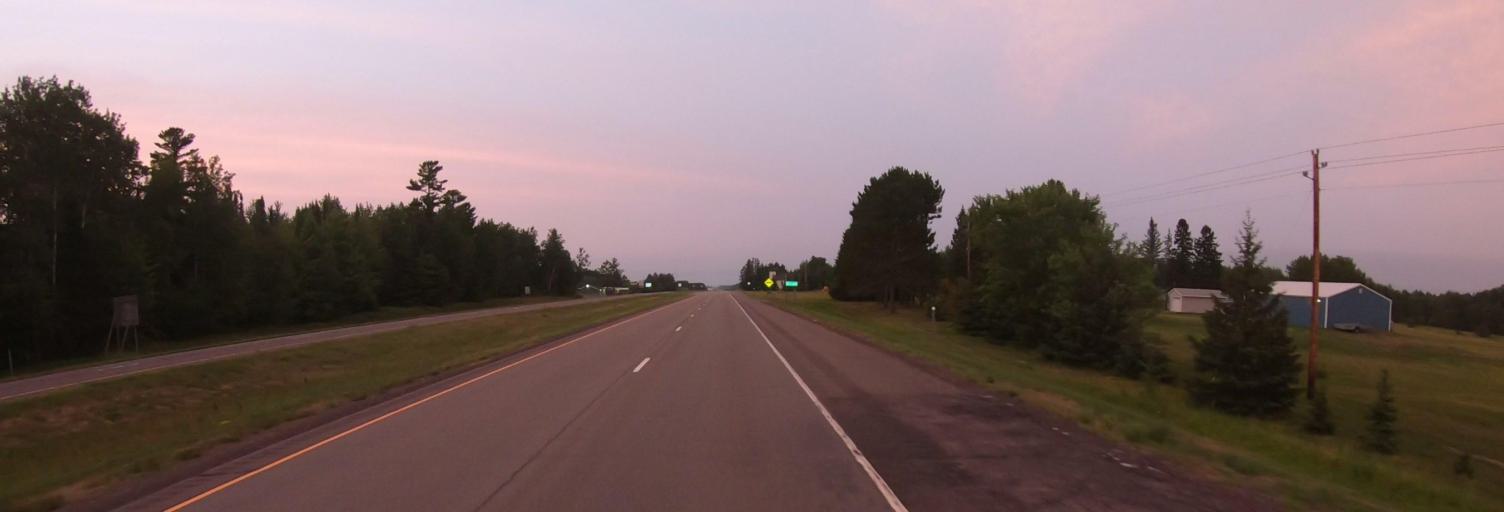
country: US
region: Minnesota
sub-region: Carlton County
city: Cloquet
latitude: 47.0329
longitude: -92.4711
